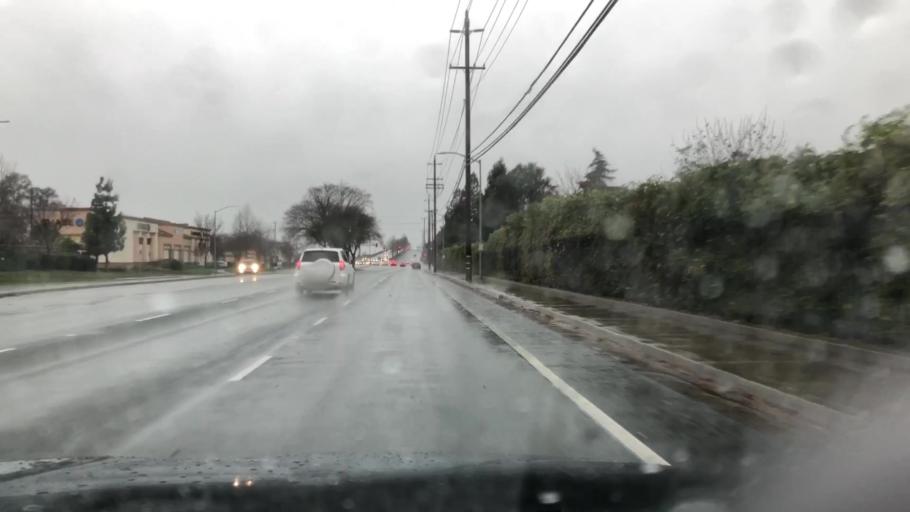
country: US
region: California
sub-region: Sacramento County
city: Laguna
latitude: 38.4088
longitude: -121.4464
